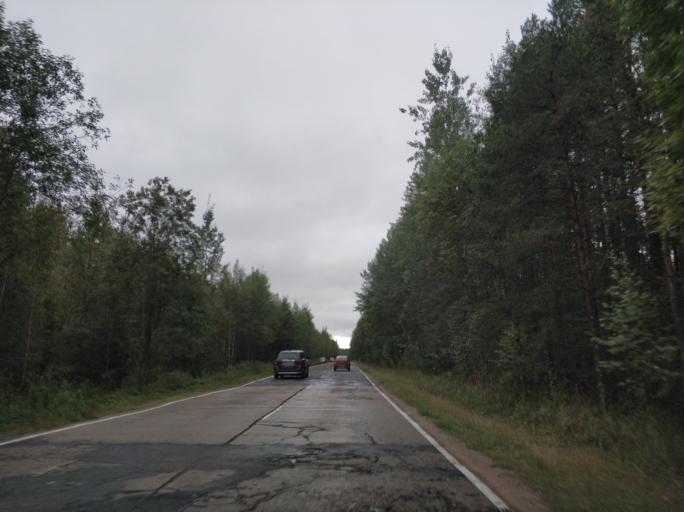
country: RU
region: Leningrad
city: Borisova Griva
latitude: 60.1729
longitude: 30.9195
